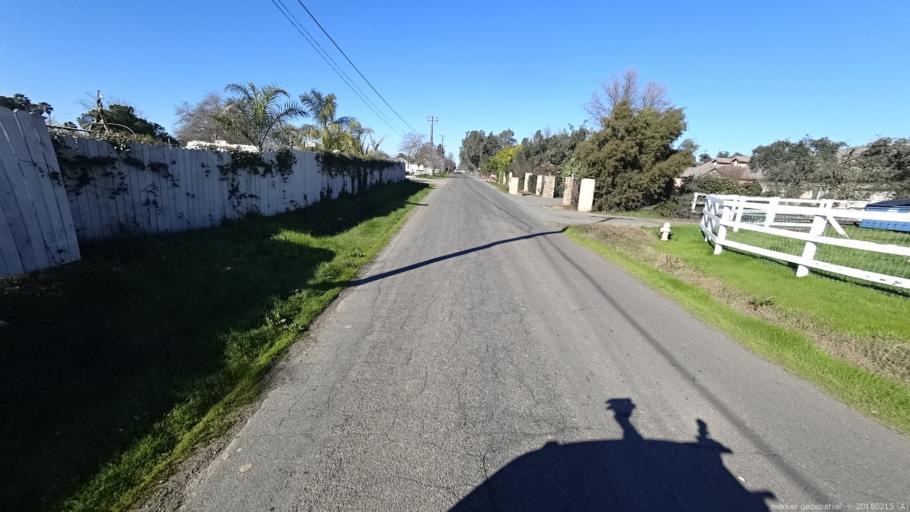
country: US
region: California
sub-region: Sacramento County
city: Rio Linda
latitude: 38.6784
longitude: -121.4615
